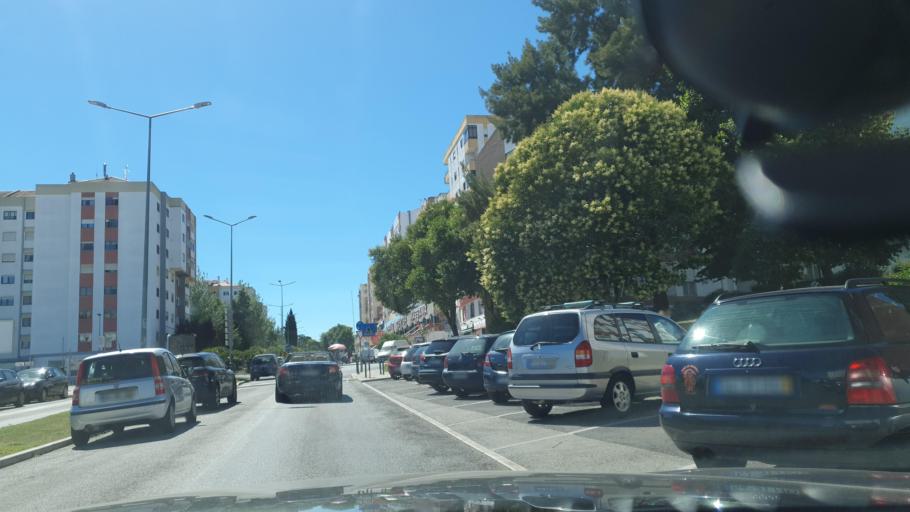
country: PT
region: Lisbon
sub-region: Oeiras
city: Barcarena
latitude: 38.7524
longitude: -9.2831
